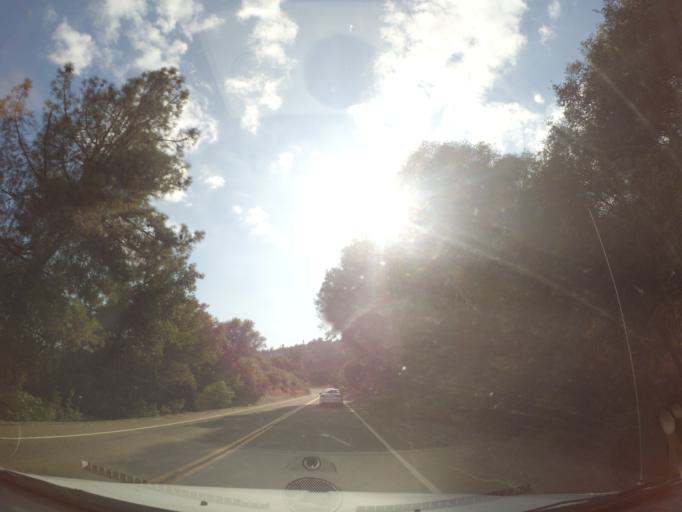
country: US
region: California
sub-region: Mariposa County
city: Mariposa
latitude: 37.5136
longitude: -119.9608
